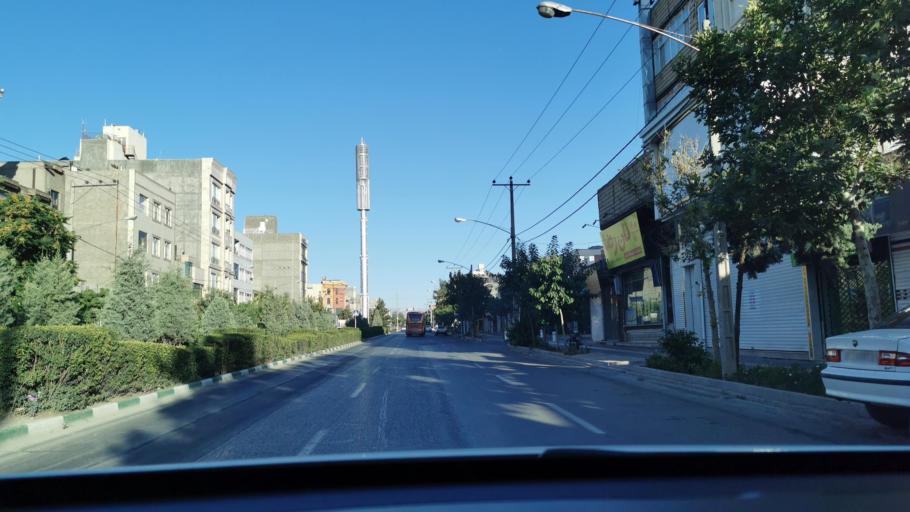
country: IR
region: Razavi Khorasan
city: Mashhad
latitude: 36.3521
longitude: 59.5038
